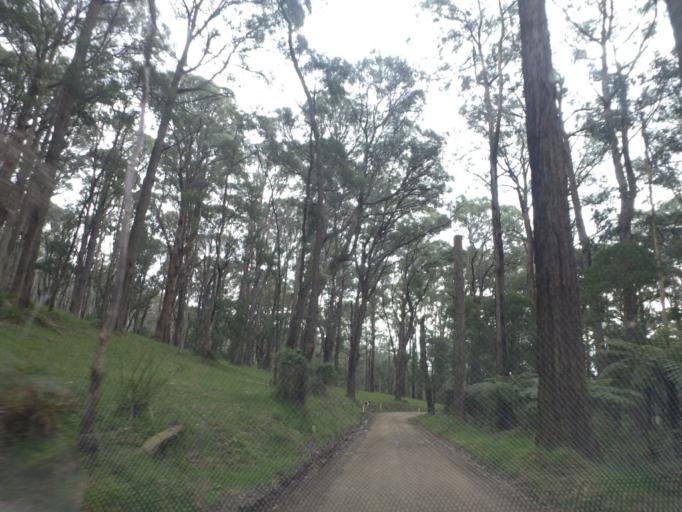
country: AU
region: Victoria
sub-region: Yarra Ranges
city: Olinda
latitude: -37.8594
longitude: 145.3473
